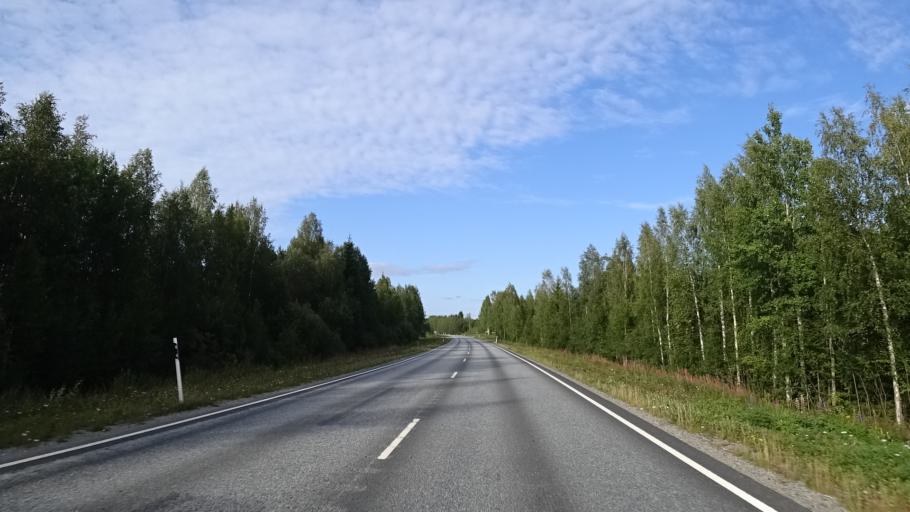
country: FI
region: North Karelia
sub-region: Joensuu
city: Eno
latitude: 62.8165
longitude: 30.1833
